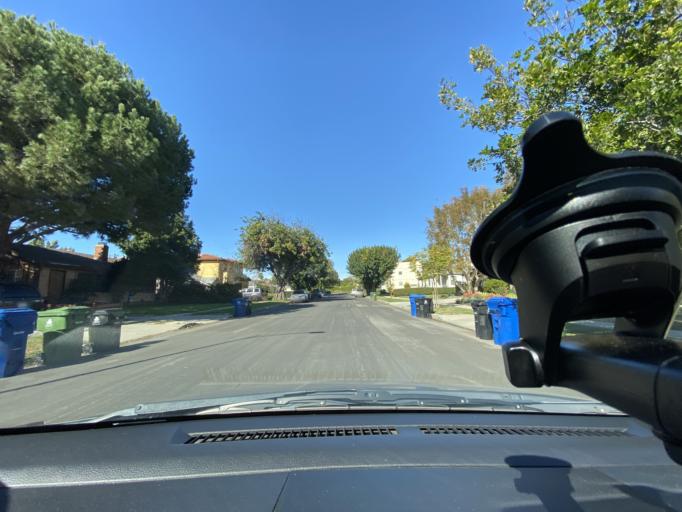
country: US
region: California
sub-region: Los Angeles County
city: Westwood, Los Angeles
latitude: 34.0353
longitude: -118.4270
